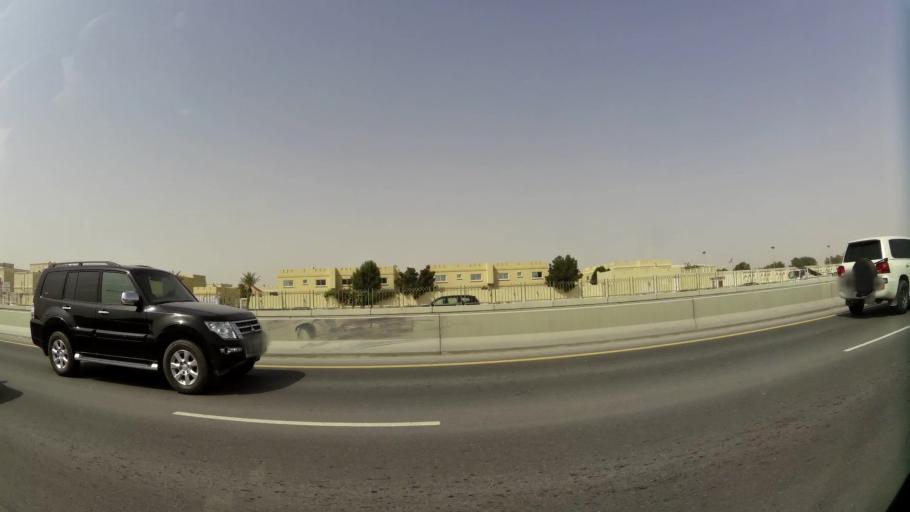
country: QA
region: Baladiyat ar Rayyan
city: Ar Rayyan
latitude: 25.3029
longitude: 51.4739
